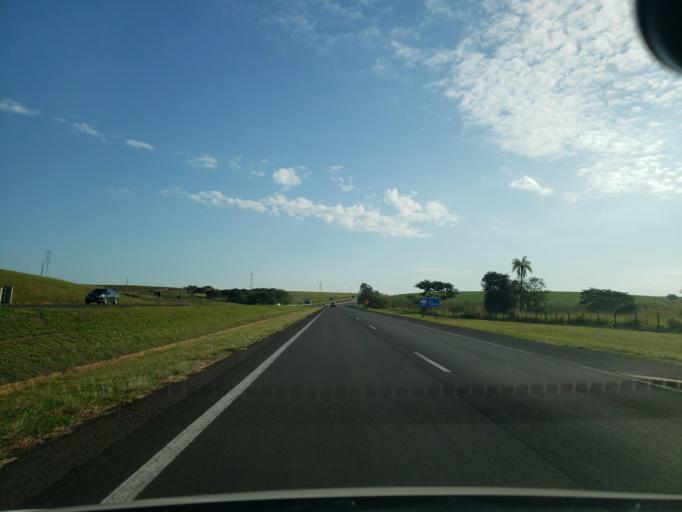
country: BR
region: Sao Paulo
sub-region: Valparaiso
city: Valparaiso
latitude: -21.2153
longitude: -50.8395
